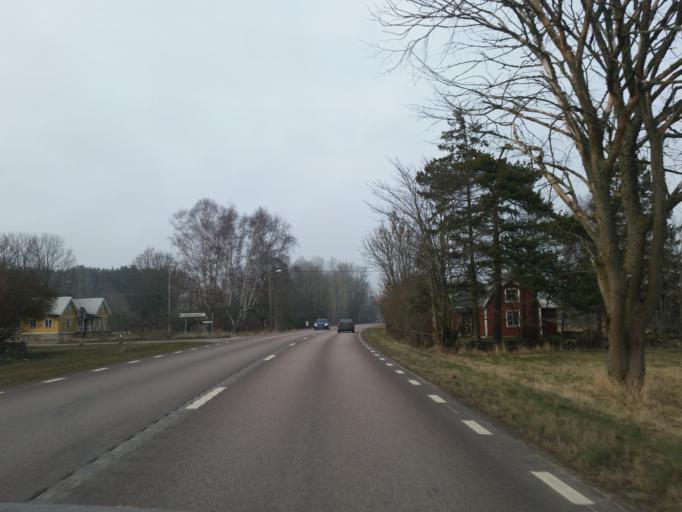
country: SE
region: Kalmar
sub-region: Borgholms Kommun
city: Borgholm
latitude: 57.1583
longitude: 17.0098
